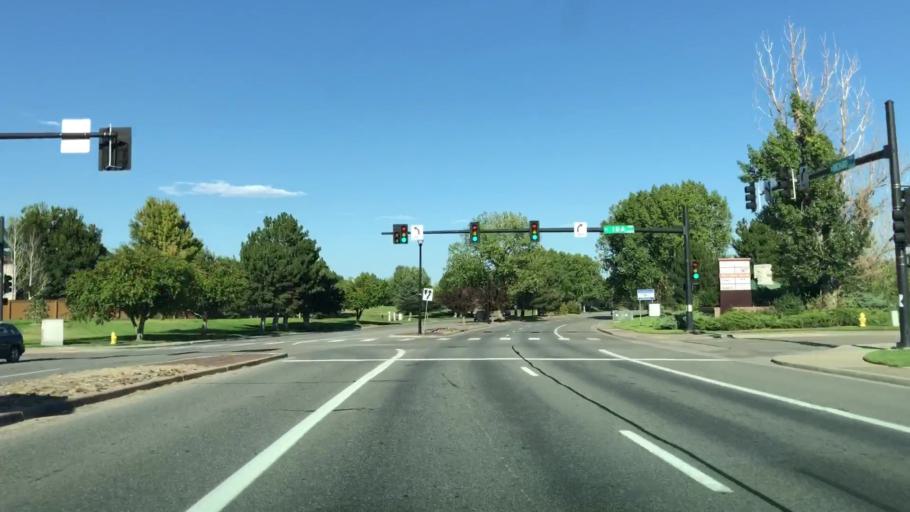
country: US
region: Colorado
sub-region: Arapahoe County
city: Dove Valley
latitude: 39.6108
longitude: -104.8090
